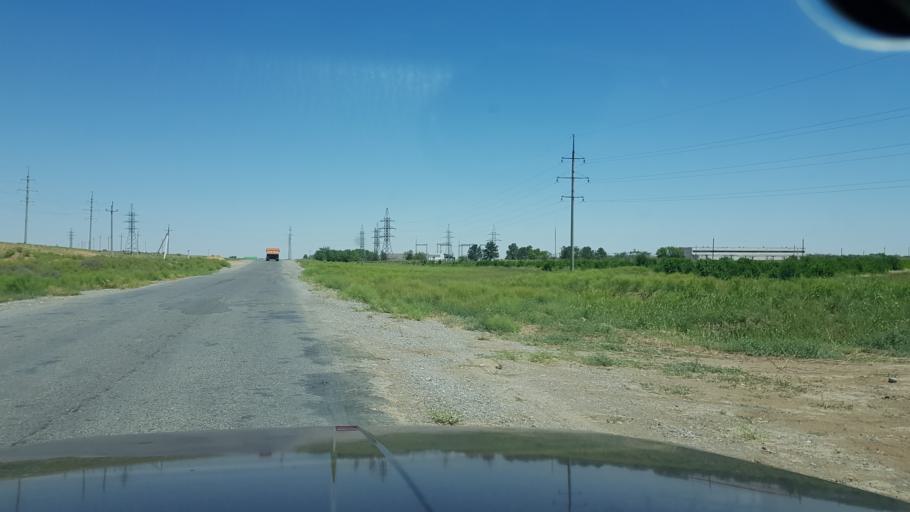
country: TM
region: Ahal
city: Annau
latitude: 37.8813
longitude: 58.7286
